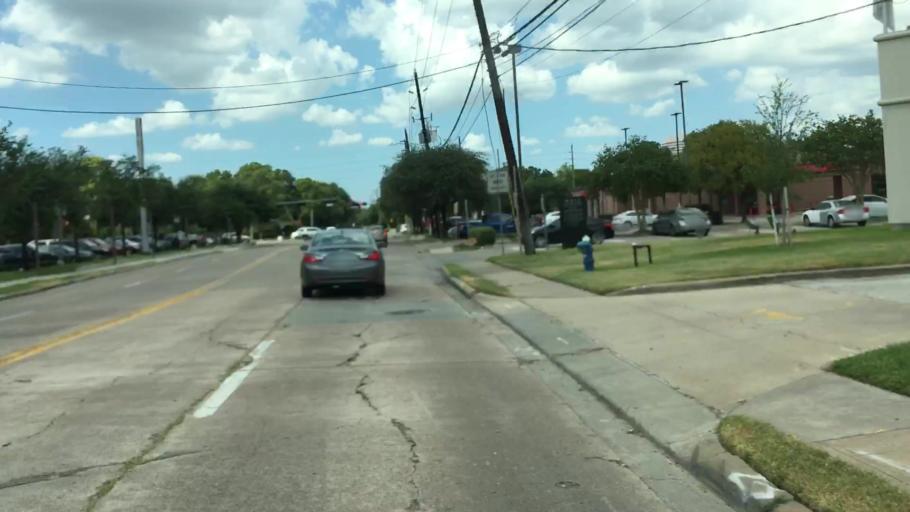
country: US
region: Texas
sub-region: Harris County
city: Hunters Creek Village
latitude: 29.7488
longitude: -95.4671
